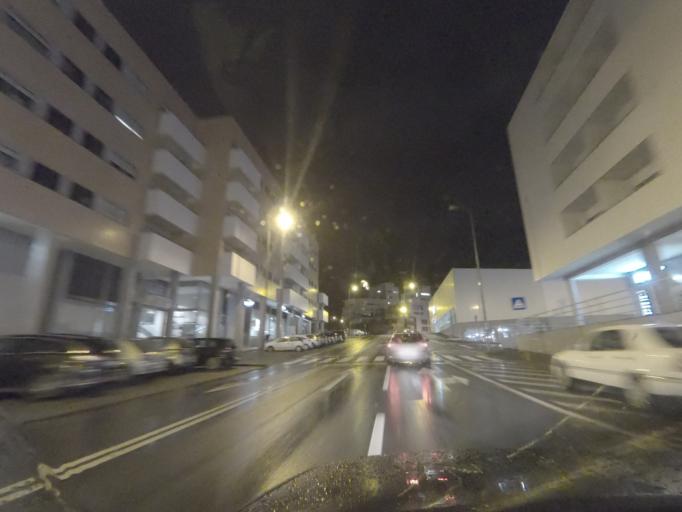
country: PT
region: Vila Real
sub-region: Vila Real
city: Vila Real
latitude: 41.2977
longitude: -7.7330
